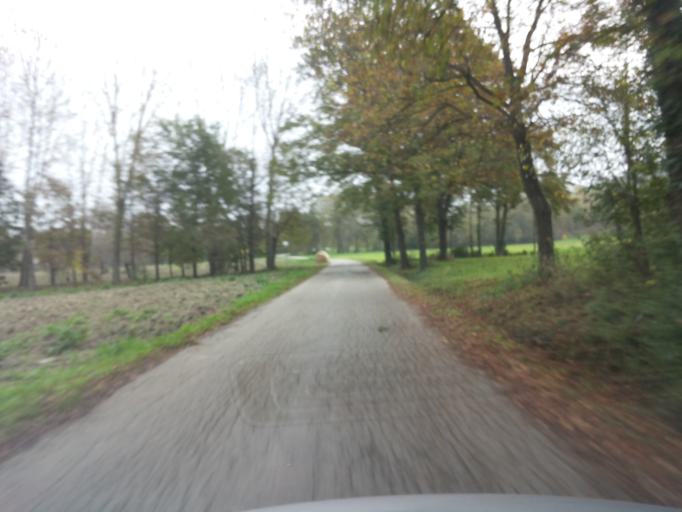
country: IT
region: Piedmont
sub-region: Provincia di Alessandria
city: Serralunga di Crea
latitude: 45.1071
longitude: 8.2763
